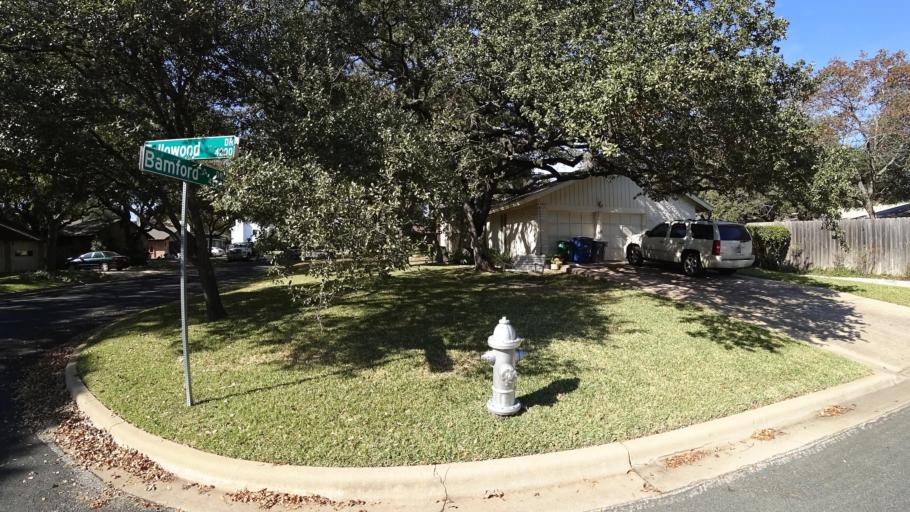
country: US
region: Texas
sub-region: Williamson County
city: Jollyville
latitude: 30.3673
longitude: -97.7649
